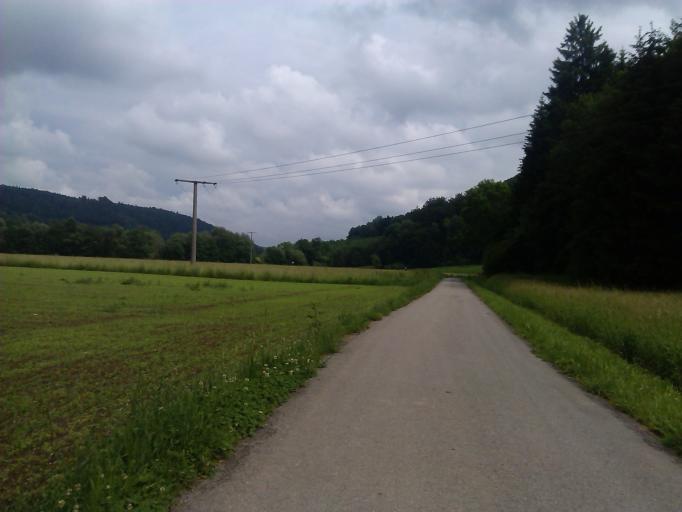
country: DE
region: Baden-Wuerttemberg
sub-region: Regierungsbezirk Stuttgart
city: Gaildorf
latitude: 48.9739
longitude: 9.8032
